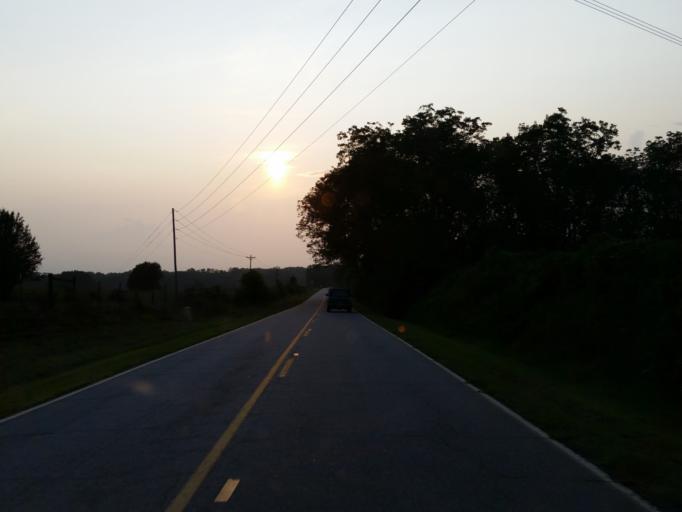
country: US
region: Georgia
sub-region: Henry County
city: Locust Grove
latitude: 33.2738
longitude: -84.1362
